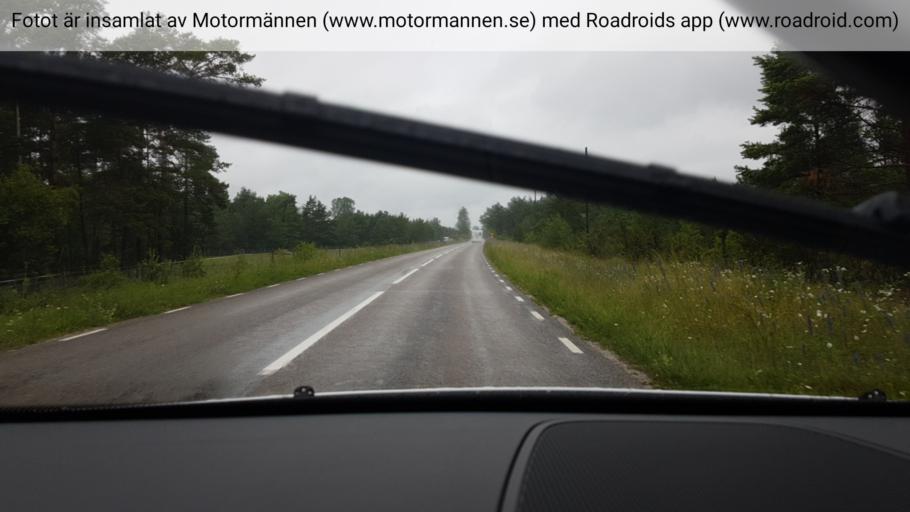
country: SE
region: Gotland
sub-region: Gotland
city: Slite
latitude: 57.6770
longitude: 18.7688
